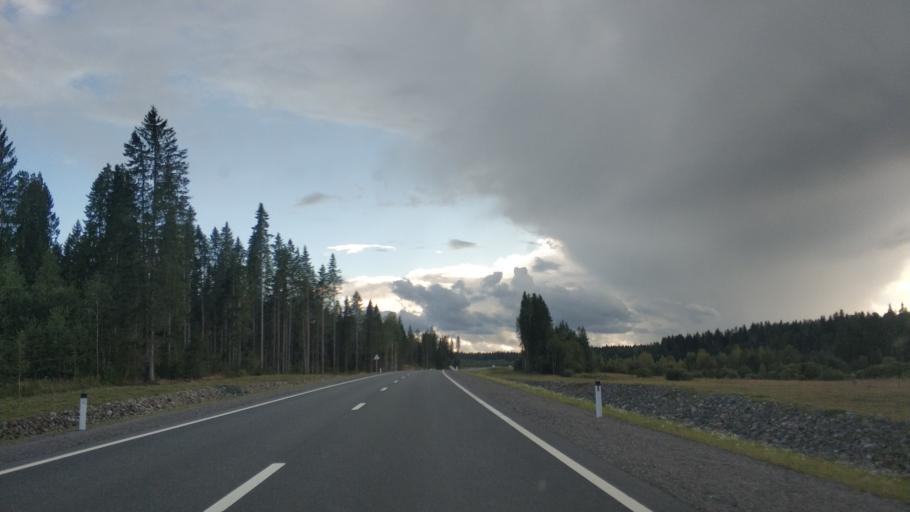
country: RU
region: Republic of Karelia
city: Lakhdenpokh'ya
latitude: 61.4519
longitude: 29.9963
